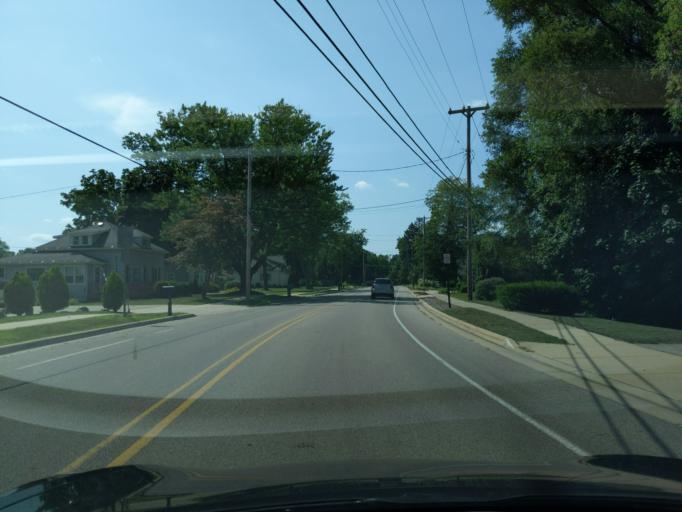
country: US
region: Michigan
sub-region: Eaton County
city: Grand Ledge
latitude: 42.7473
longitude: -84.7370
